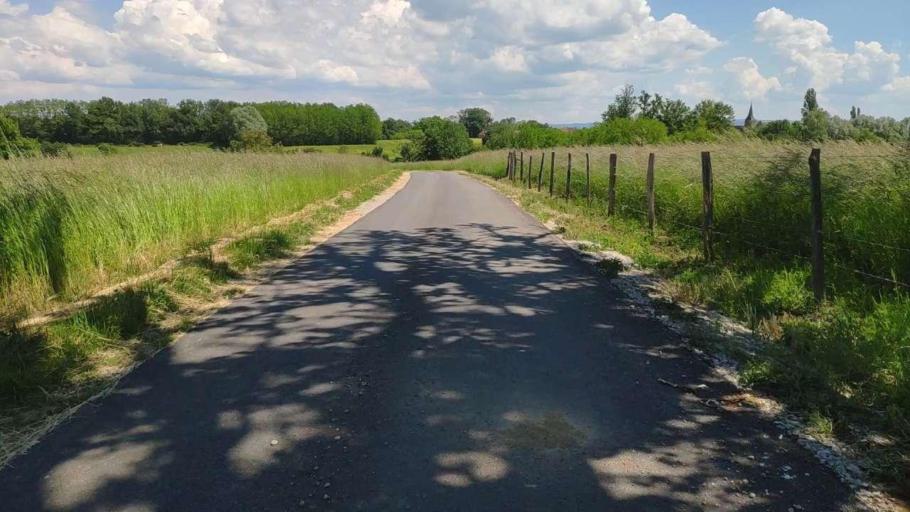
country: FR
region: Franche-Comte
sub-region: Departement du Jura
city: Bletterans
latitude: 46.7541
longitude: 5.3978
